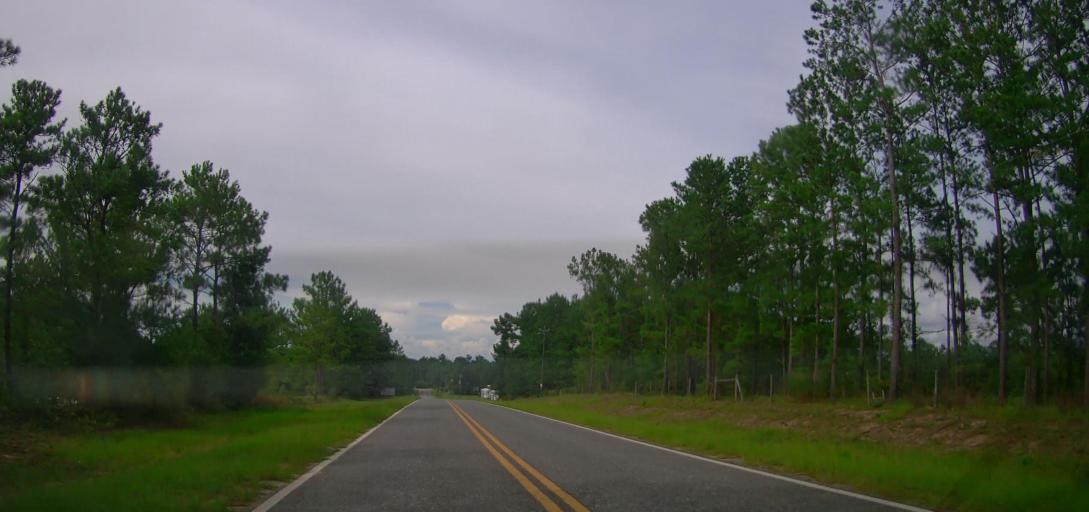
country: US
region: Georgia
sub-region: Wayne County
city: Jesup
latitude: 31.6725
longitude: -81.9079
